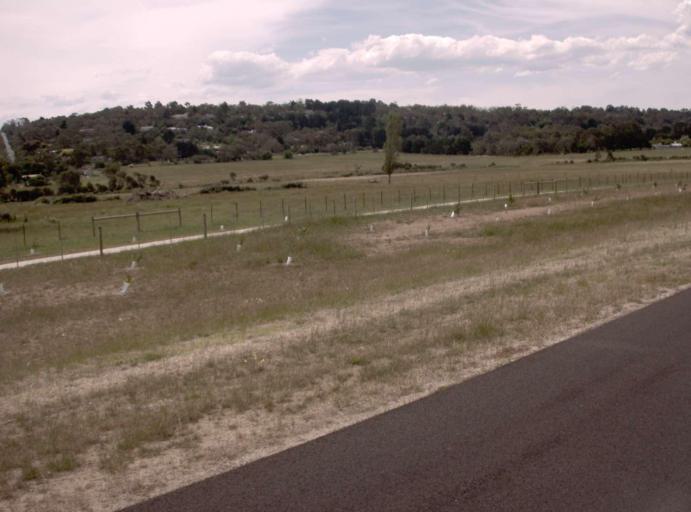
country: AU
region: Victoria
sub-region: Mornington Peninsula
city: Baxter
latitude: -38.2060
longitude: 145.1332
